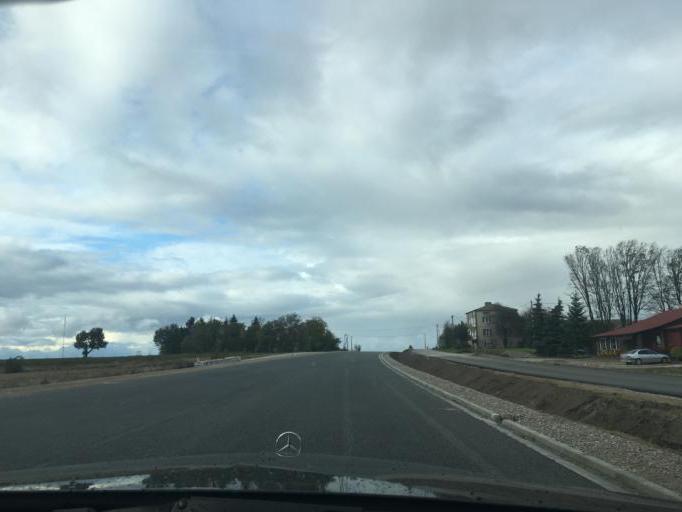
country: PL
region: Lublin Voivodeship
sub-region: Powiat lubelski
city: Krzczonow
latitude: 50.9850
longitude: 22.6783
